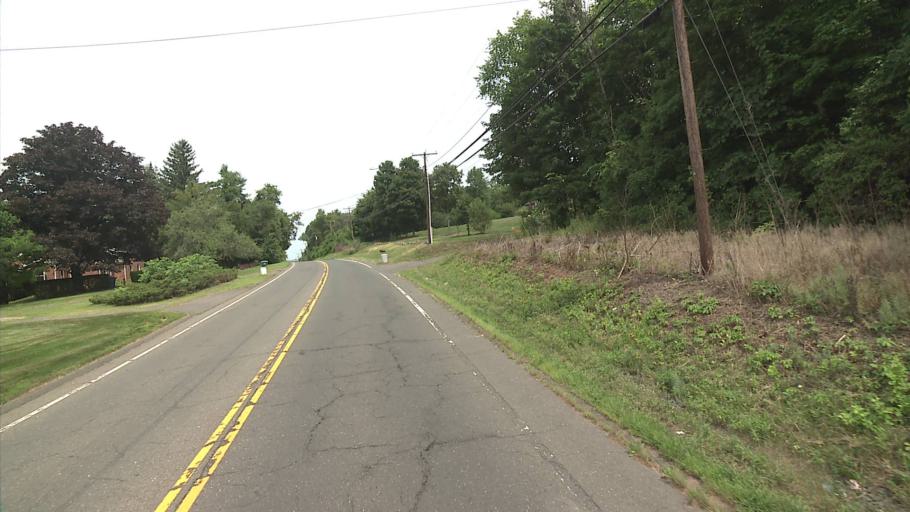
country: US
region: Connecticut
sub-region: Hartford County
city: Kensington
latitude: 41.5928
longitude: -72.7986
